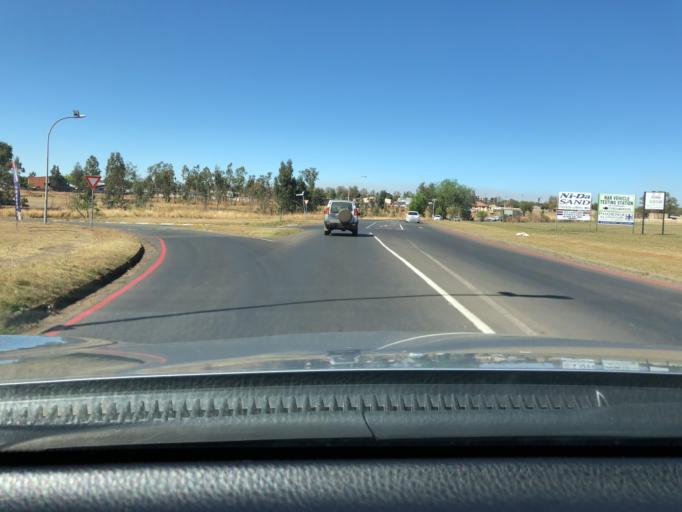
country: ZA
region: KwaZulu-Natal
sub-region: Amajuba District Municipality
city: Newcastle
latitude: -27.7604
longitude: 29.9455
